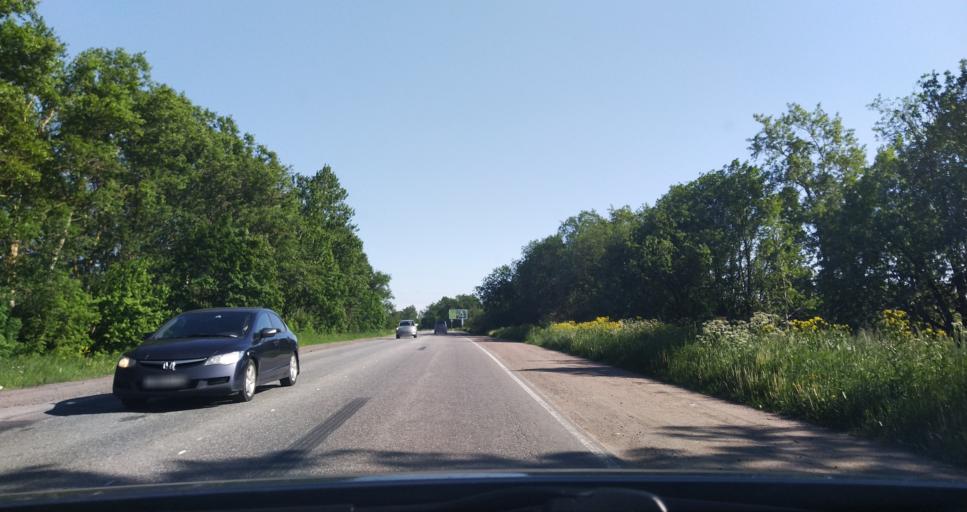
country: RU
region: St.-Petersburg
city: Krasnoye Selo
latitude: 59.7130
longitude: 30.0834
